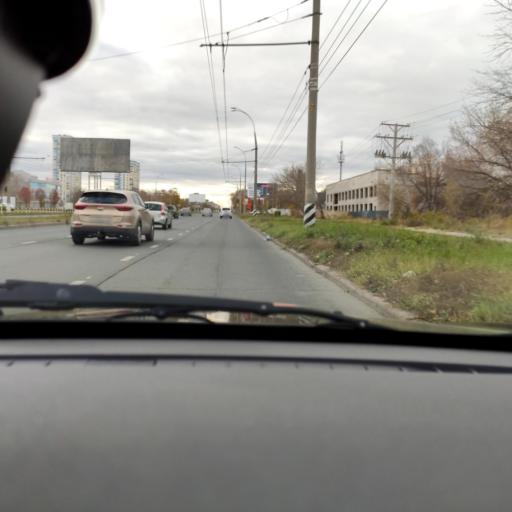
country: RU
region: Samara
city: Tol'yatti
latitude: 53.5472
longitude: 49.3016
